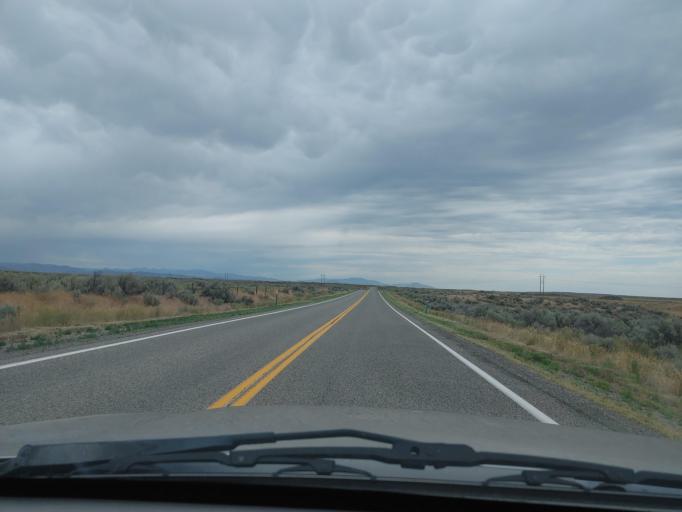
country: US
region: Idaho
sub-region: Lincoln County
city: Shoshone
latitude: 43.0833
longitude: -114.0994
